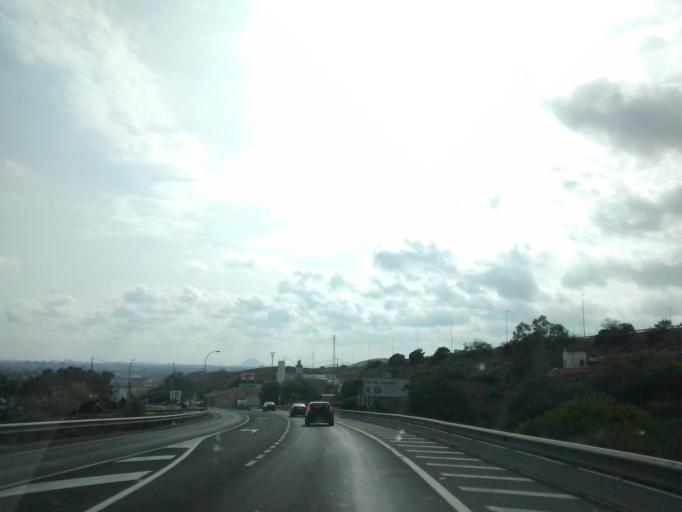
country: ES
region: Valencia
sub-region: Provincia de Alicante
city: el Campello
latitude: 38.4544
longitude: -0.3680
